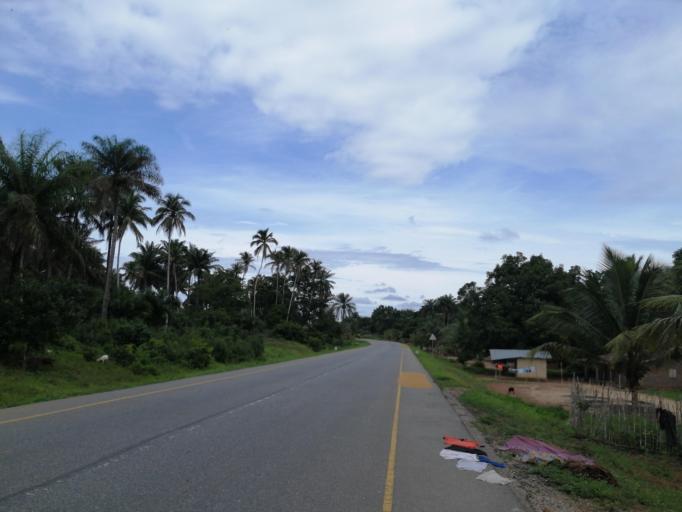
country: SL
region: Northern Province
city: Port Loko
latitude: 8.7639
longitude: -12.9073
